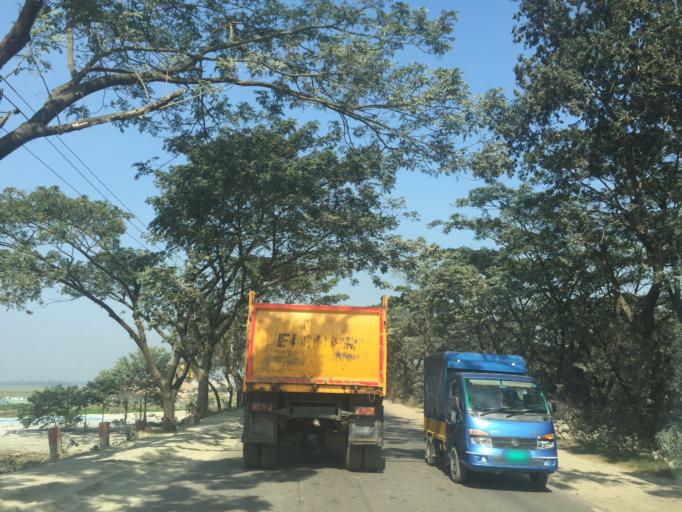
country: BD
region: Dhaka
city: Tungi
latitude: 23.8319
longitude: 90.3405
